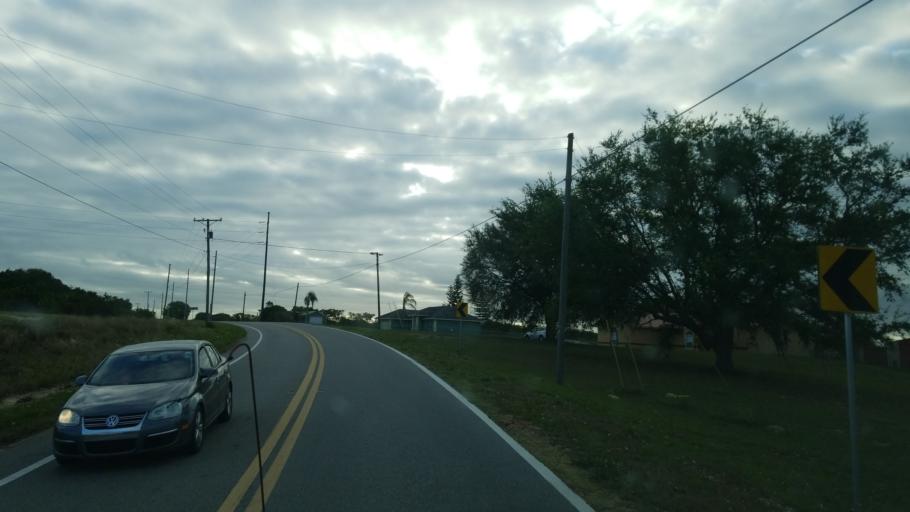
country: US
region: Florida
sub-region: Polk County
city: Lake Wales
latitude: 27.9611
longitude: -81.5799
